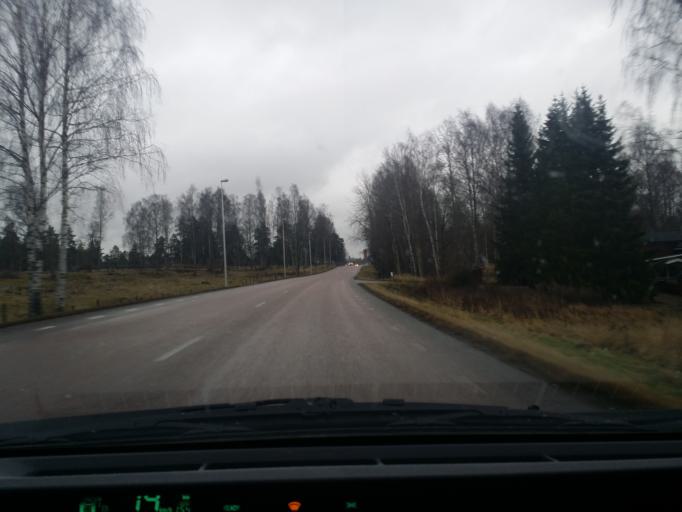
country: SE
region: Vaestmanland
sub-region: Sala Kommun
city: Sala
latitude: 59.9018
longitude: 16.5766
